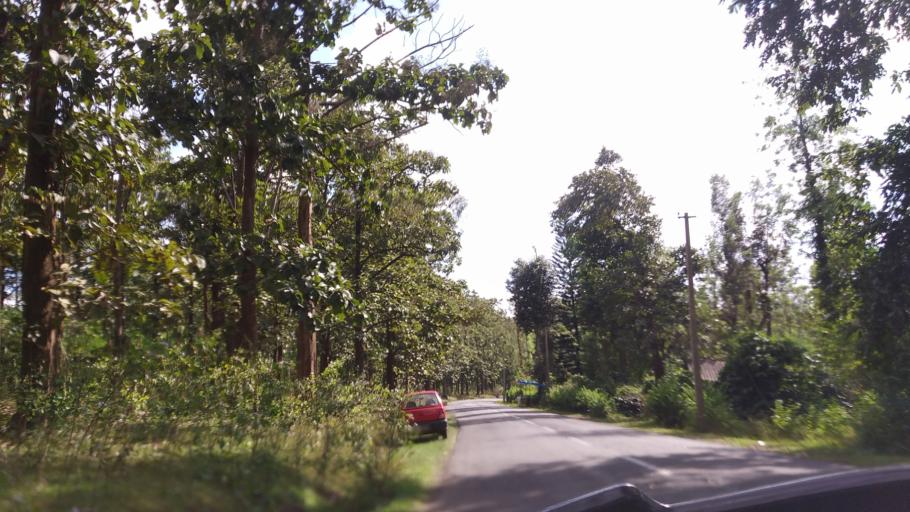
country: IN
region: Kerala
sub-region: Wayanad
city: Panamaram
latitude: 11.9383
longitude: 76.0646
